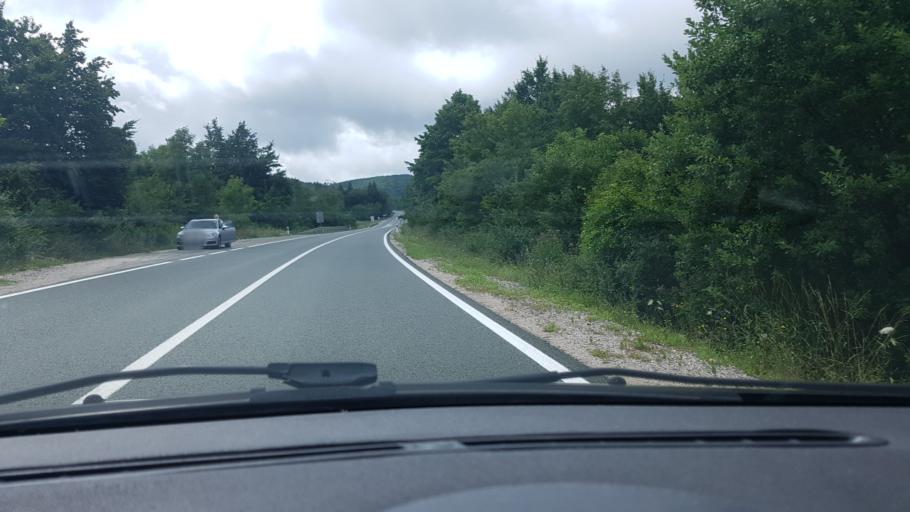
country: HR
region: Licko-Senjska
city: Jezerce
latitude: 44.8437
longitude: 15.6799
